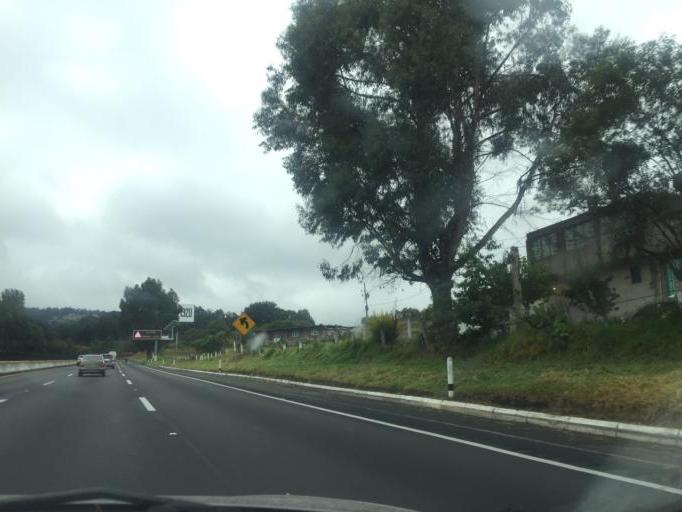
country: MX
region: Mexico City
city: Xochimilco
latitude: 19.1950
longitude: -99.1545
